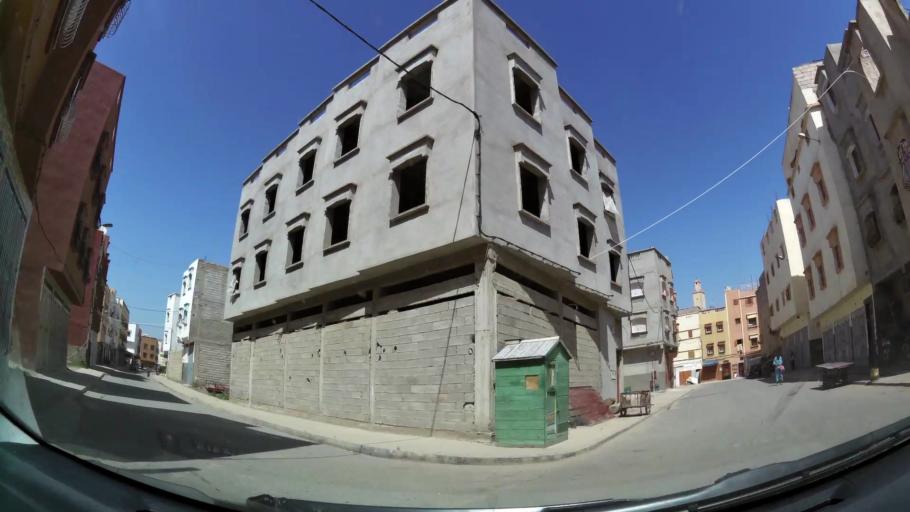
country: MA
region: Souss-Massa-Draa
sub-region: Inezgane-Ait Mellou
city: Inezgane
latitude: 30.3459
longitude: -9.5371
